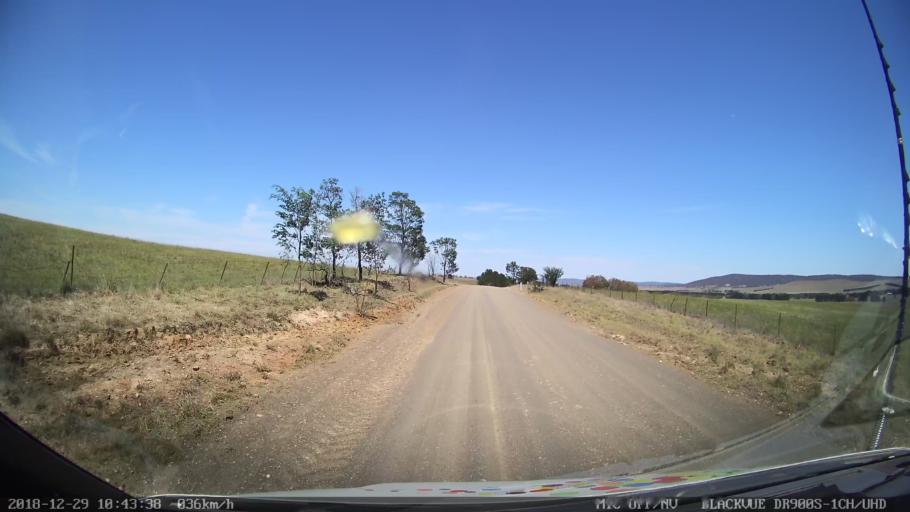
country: AU
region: New South Wales
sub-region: Palerang
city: Bungendore
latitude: -35.0408
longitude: 149.5360
